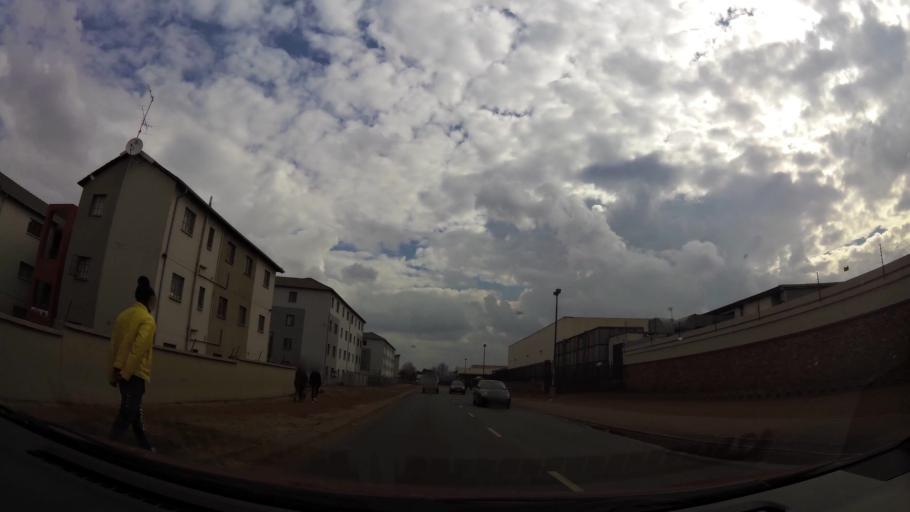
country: ZA
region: Gauteng
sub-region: City of Johannesburg Metropolitan Municipality
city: Soweto
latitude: -26.2518
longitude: 27.8579
